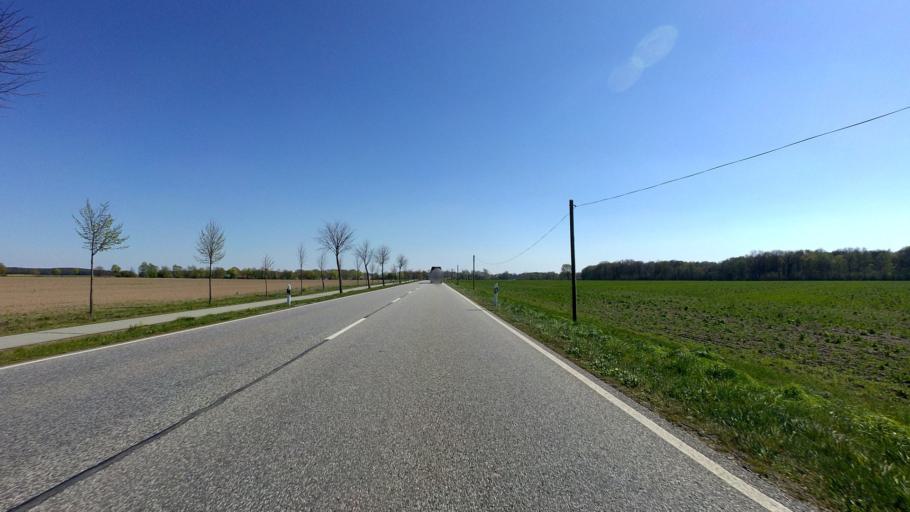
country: DE
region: Saxony-Anhalt
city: Pretzier
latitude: 52.8061
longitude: 11.2245
